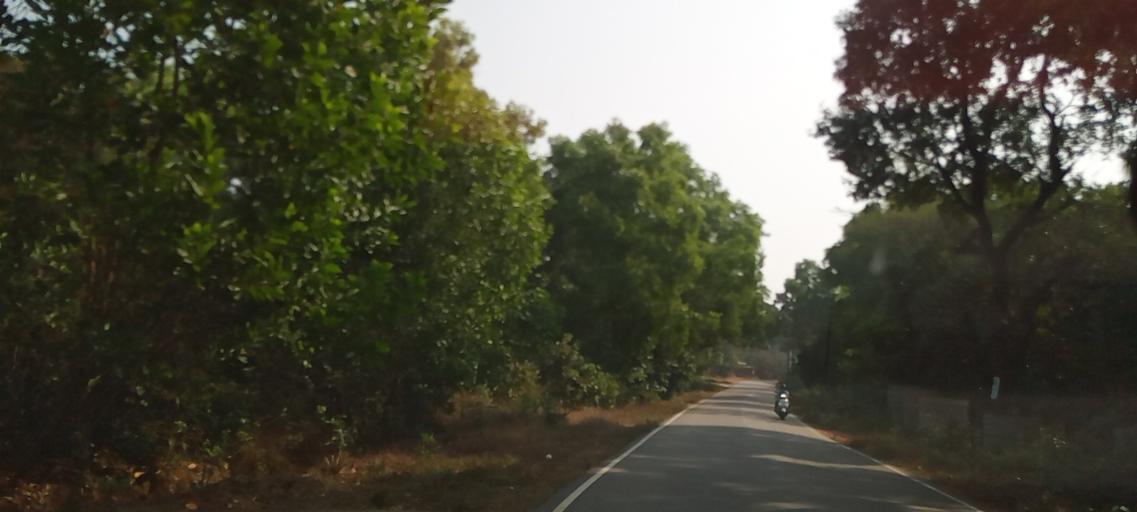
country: IN
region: Karnataka
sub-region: Udupi
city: Coondapoor
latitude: 13.5158
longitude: 74.7877
